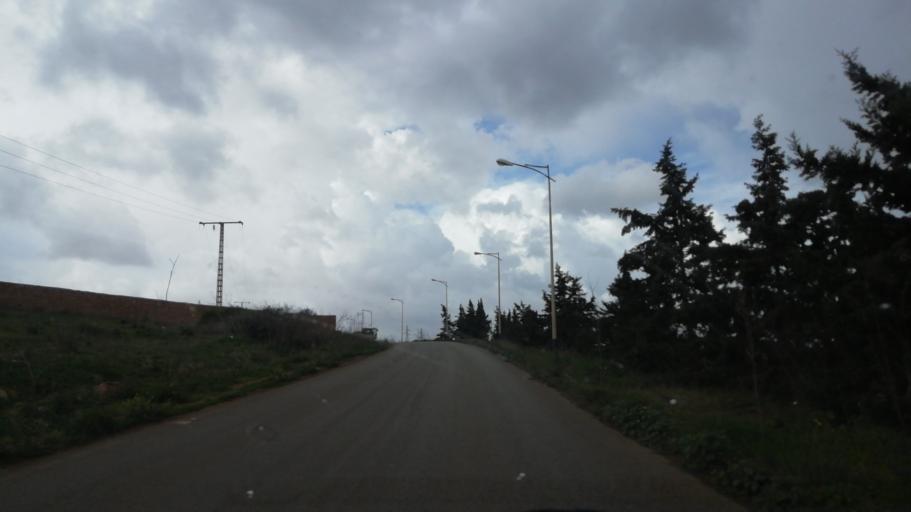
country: DZ
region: Oran
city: Sidi ech Chahmi
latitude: 35.6283
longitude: -0.5260
